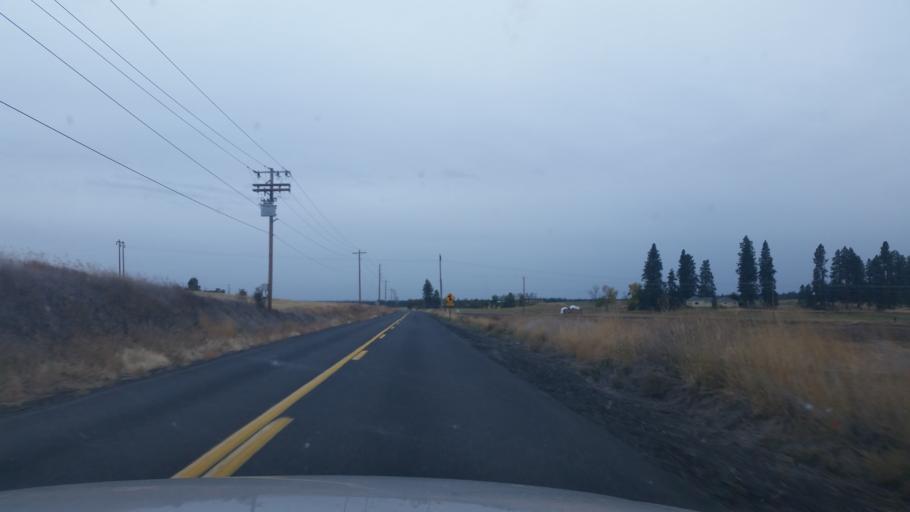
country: US
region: Washington
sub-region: Spokane County
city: Cheney
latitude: 47.5310
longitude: -117.5505
